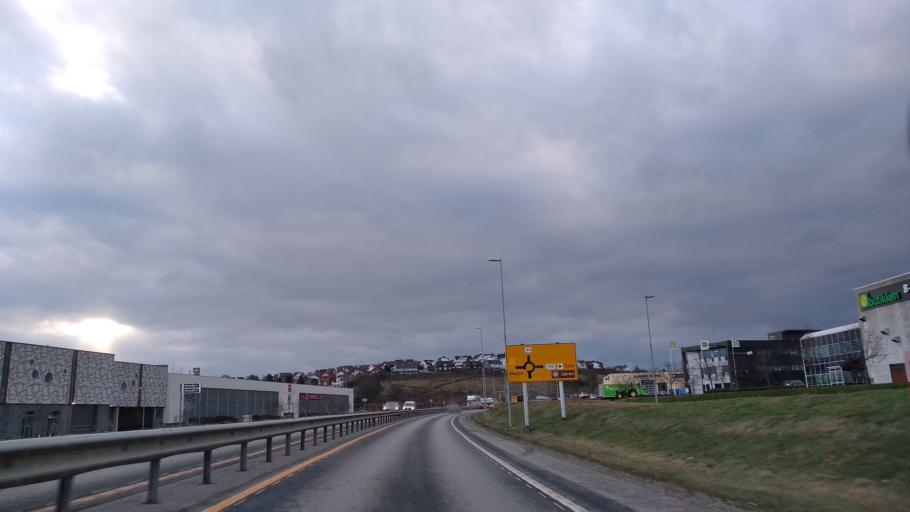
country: NO
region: Rogaland
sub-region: Klepp
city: Kleppe
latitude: 58.7814
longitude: 5.6263
